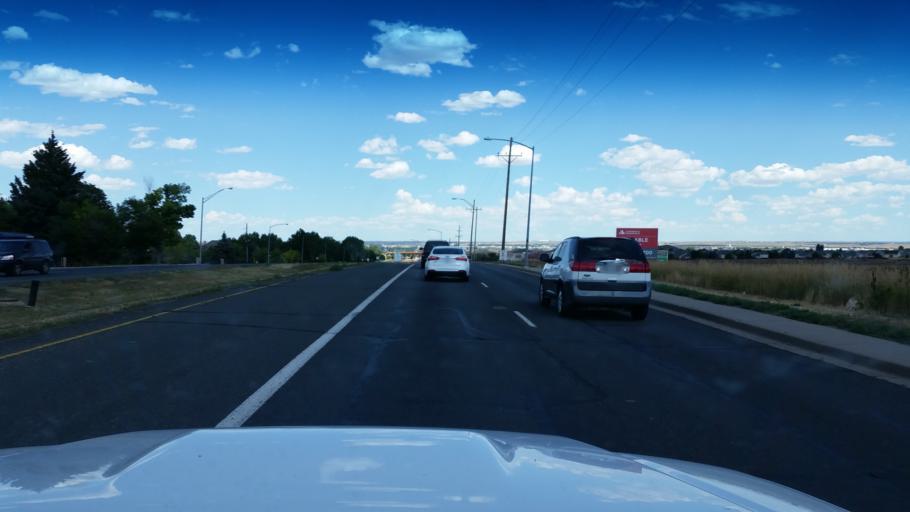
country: US
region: Colorado
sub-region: Adams County
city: Thornton
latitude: 39.8848
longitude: -104.9566
